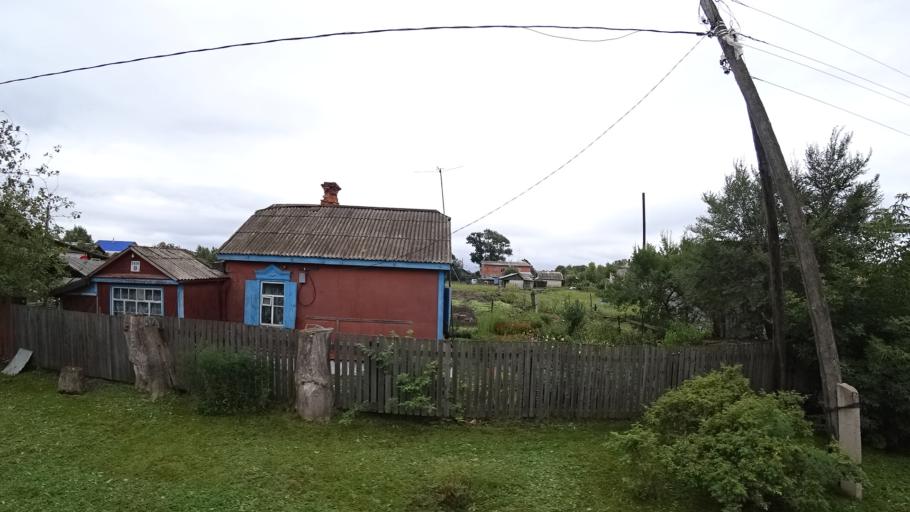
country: RU
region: Primorskiy
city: Chernigovka
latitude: 44.3473
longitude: 132.5758
